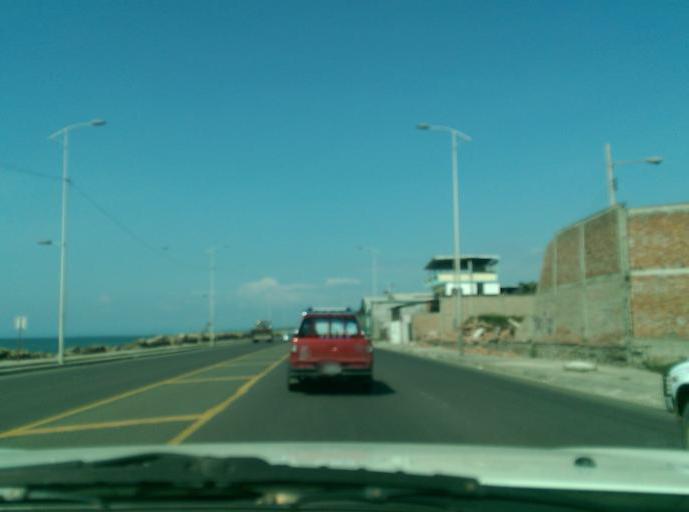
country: EC
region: Manabi
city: Manta
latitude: -0.9490
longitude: -80.7020
